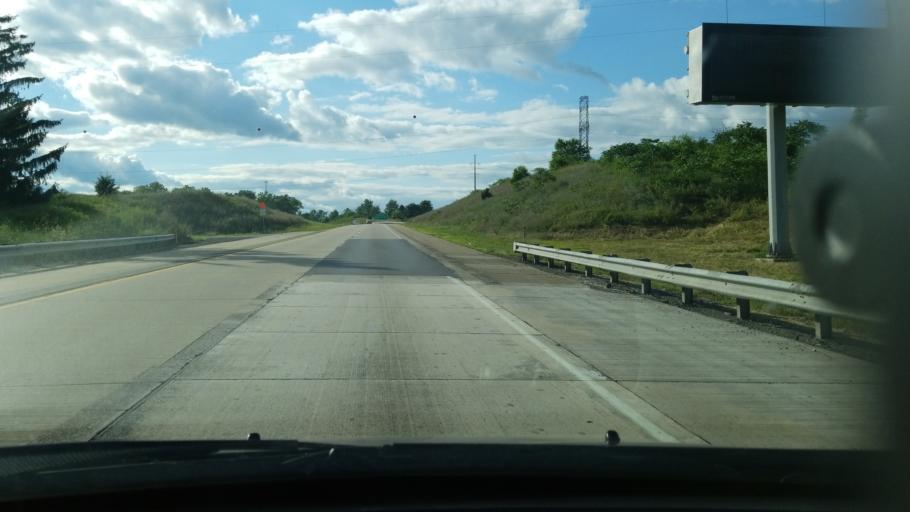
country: US
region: Pennsylvania
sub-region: Northumberland County
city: Milton
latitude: 40.9994
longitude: -76.7479
